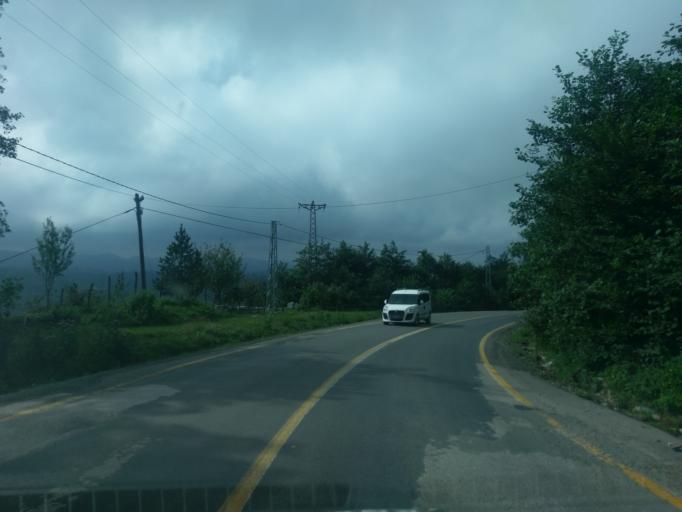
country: TR
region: Ordu
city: Gurgentepe
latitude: 40.8482
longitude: 37.6547
